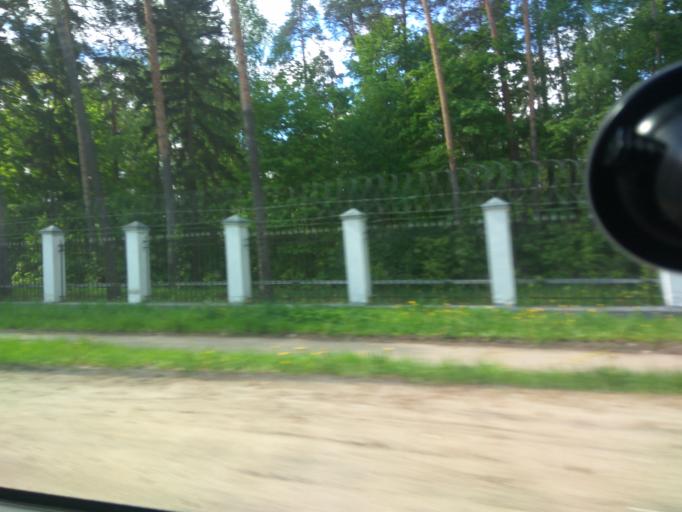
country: RU
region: Moskovskaya
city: Kratovo
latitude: 55.5797
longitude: 38.1535
